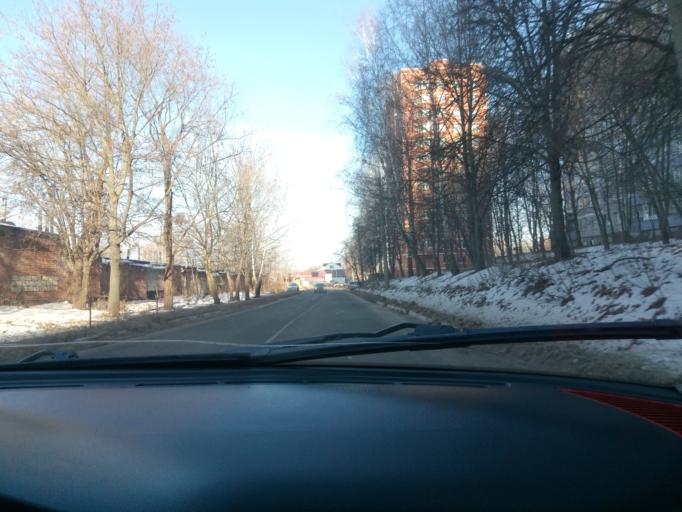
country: RU
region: Tula
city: Mendeleyevskiy
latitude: 54.1665
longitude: 37.5615
